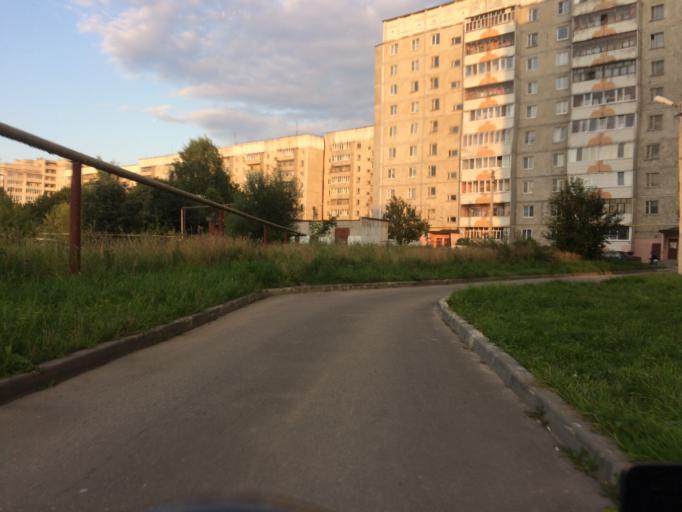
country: RU
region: Mariy-El
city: Yoshkar-Ola
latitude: 56.6436
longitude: 47.8502
